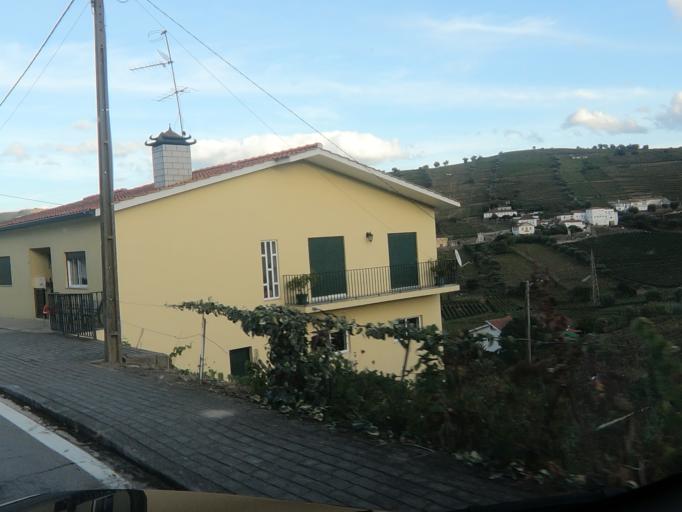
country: PT
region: Vila Real
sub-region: Santa Marta de Penaguiao
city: Santa Marta de Penaguiao
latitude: 41.1960
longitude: -7.7779
